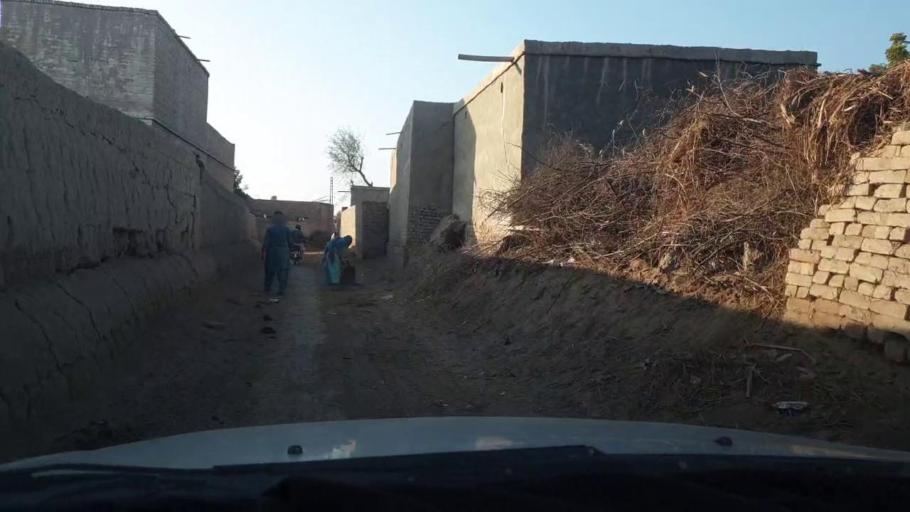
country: PK
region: Sindh
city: Mirpur Mathelo
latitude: 27.9986
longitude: 69.5157
